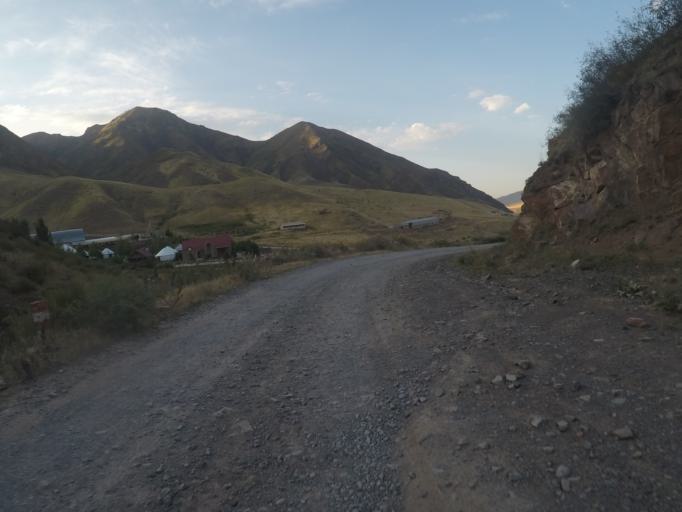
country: KG
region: Chuy
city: Bishkek
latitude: 42.6700
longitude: 74.6453
